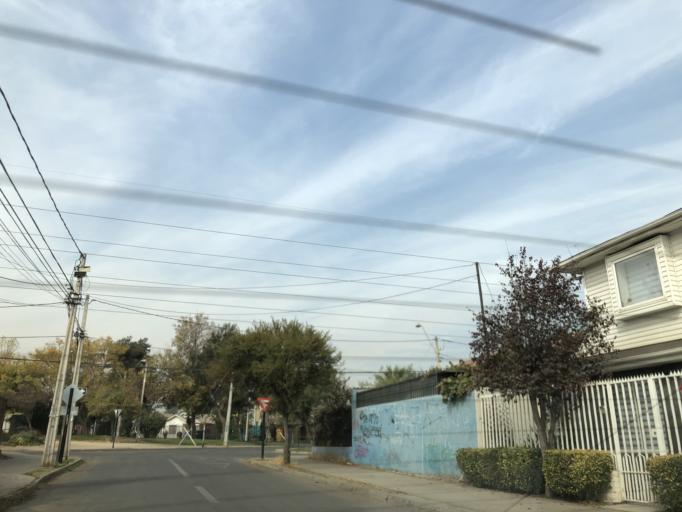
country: CL
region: Santiago Metropolitan
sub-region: Provincia de Cordillera
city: Puente Alto
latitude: -33.5647
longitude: -70.5604
